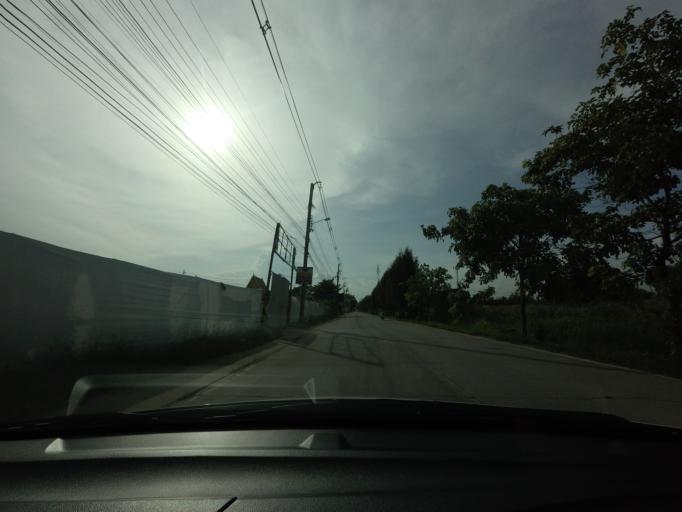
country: TH
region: Bangkok
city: Bang Na
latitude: 13.6495
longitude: 100.6583
